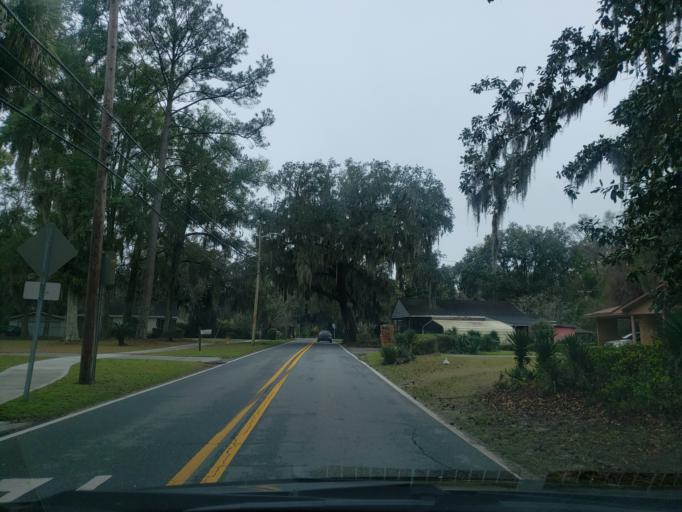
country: US
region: Georgia
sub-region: Chatham County
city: Montgomery
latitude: 31.9459
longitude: -81.1477
